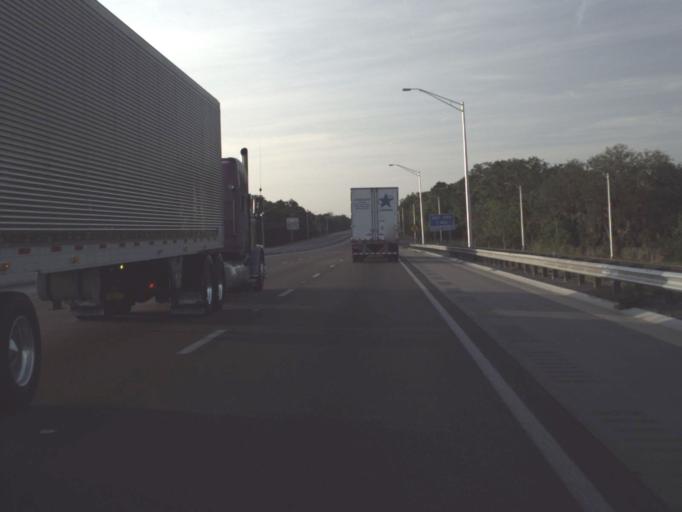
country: US
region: Florida
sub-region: Brevard County
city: Mims
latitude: 28.6680
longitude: -80.8703
